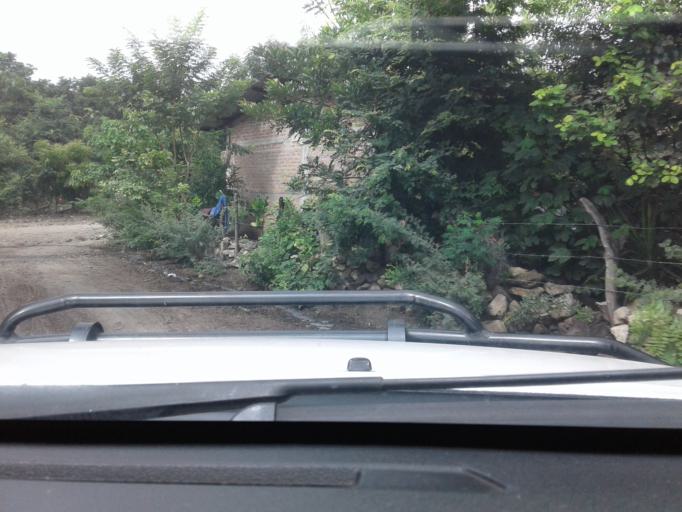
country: NI
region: Leon
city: Santa Rosa del Penon
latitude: 12.9023
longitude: -86.2103
